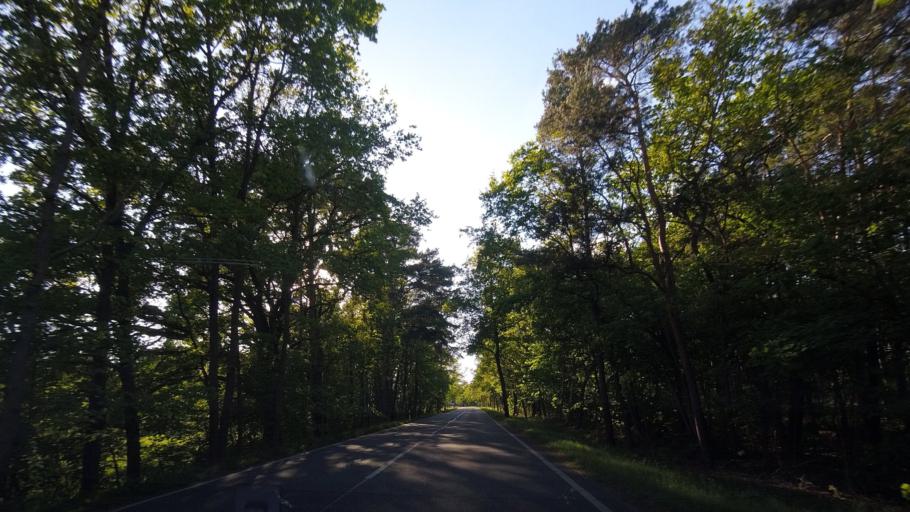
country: DE
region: Brandenburg
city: Kasel-Golzig
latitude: 51.9620
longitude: 13.7283
